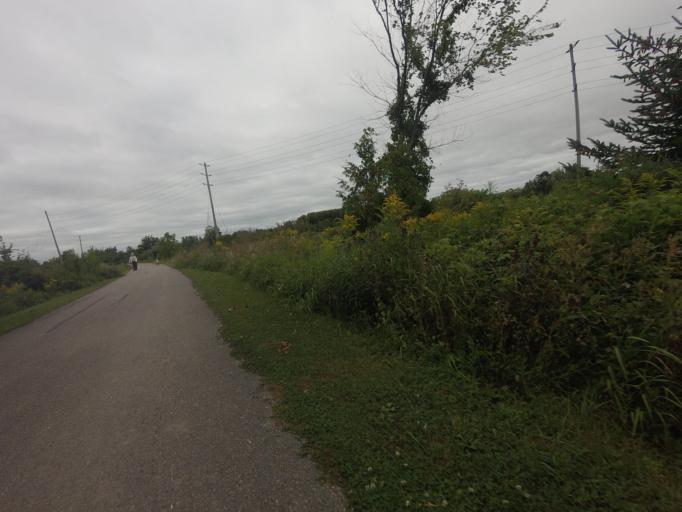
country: CA
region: Ontario
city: Omemee
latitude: 44.3738
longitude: -78.7447
